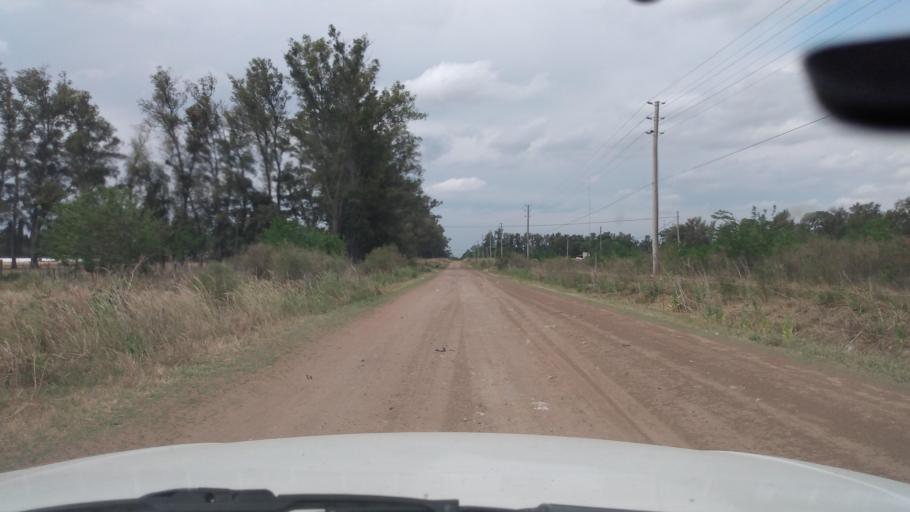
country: AR
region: Buenos Aires
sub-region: Partido de Lujan
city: Lujan
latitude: -34.5555
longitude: -59.1780
